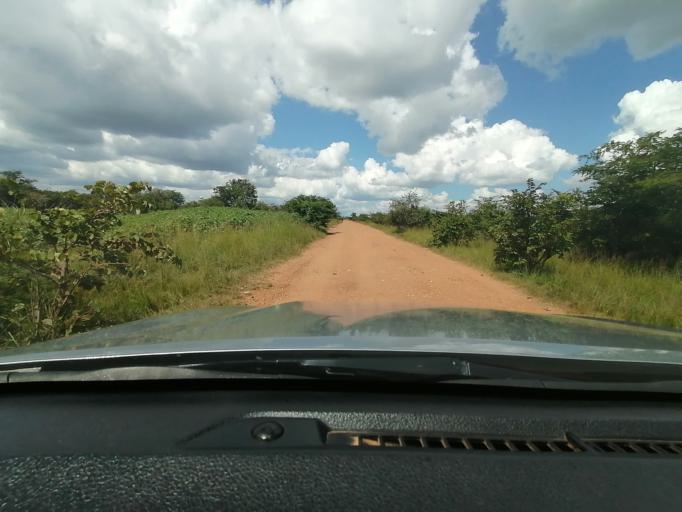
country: ZM
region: Lusaka
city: Lusaka
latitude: -15.2713
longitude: 27.7650
